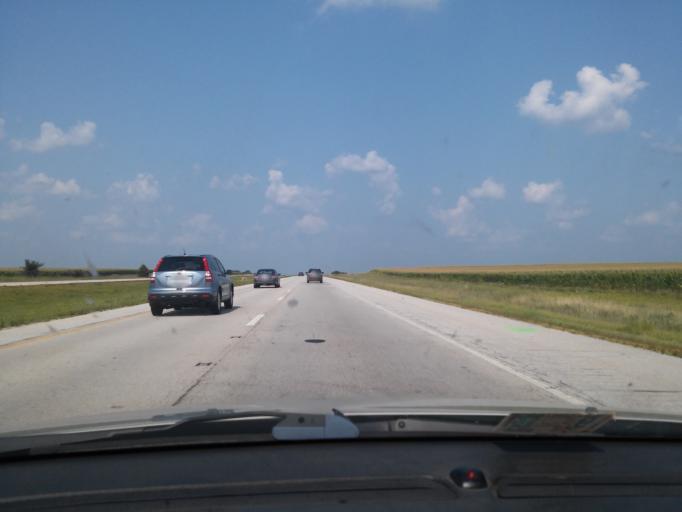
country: US
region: Illinois
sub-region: Livingston County
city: Pontiac
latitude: 40.9322
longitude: -88.6133
